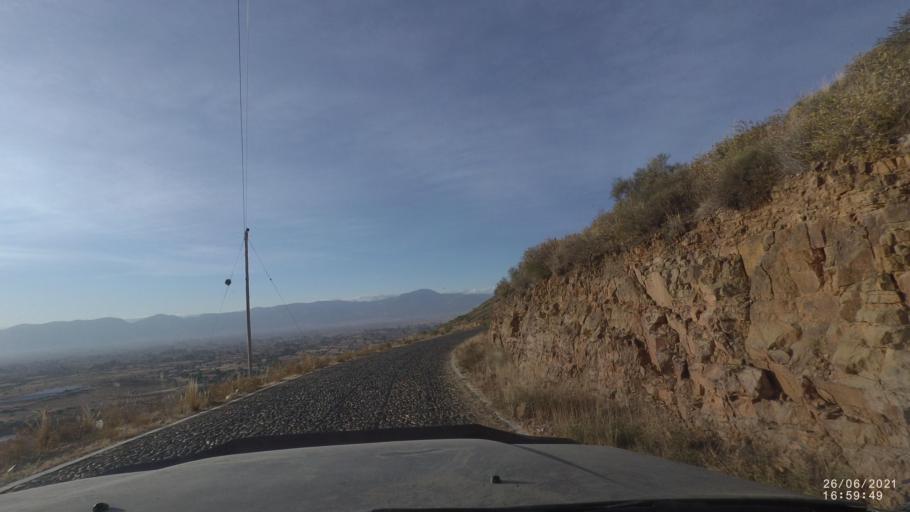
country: BO
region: Cochabamba
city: Cliza
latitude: -17.6651
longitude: -65.9091
